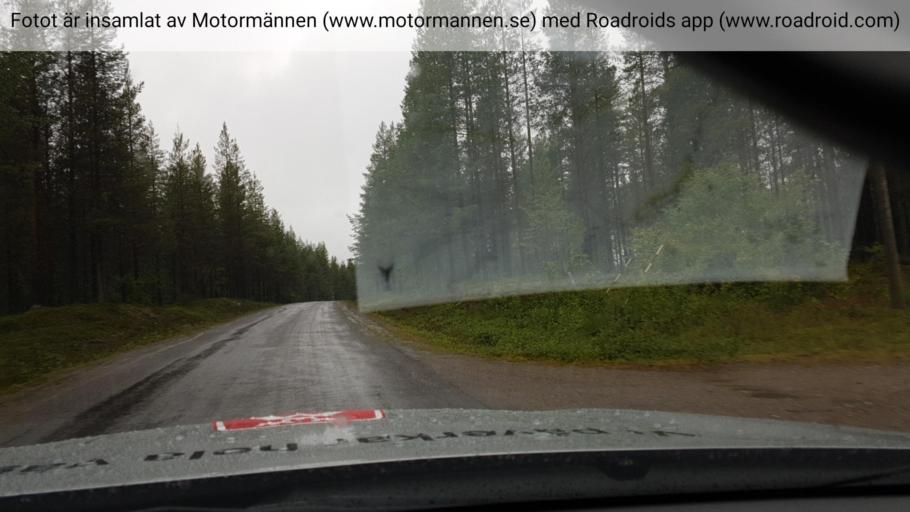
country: SE
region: Norrbotten
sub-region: Jokkmokks Kommun
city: Jokkmokk
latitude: 66.5910
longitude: 19.4068
